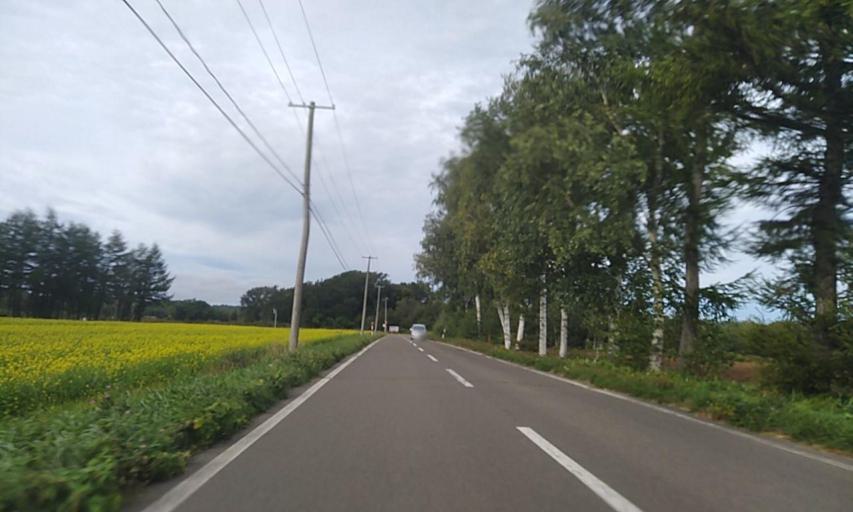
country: JP
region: Hokkaido
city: Abashiri
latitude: 43.7957
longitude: 144.5532
